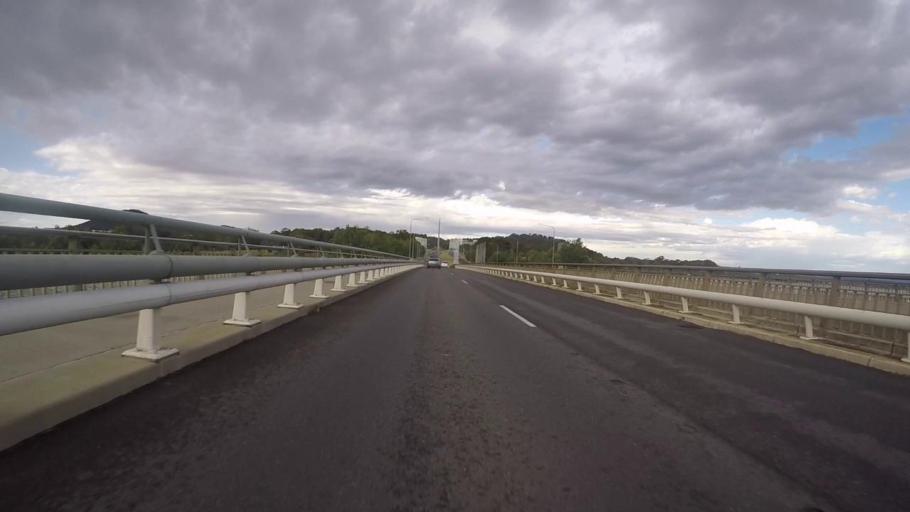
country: AU
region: Australian Capital Territory
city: Forrest
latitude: -35.3015
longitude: 149.1411
